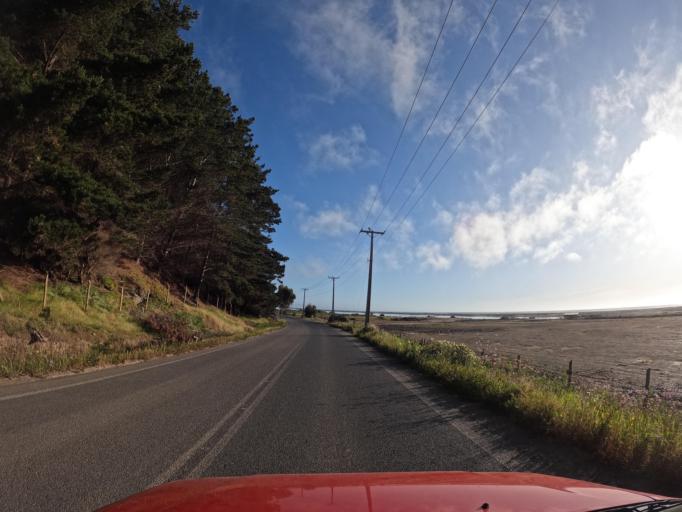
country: CL
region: Maule
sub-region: Provincia de Talca
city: Constitucion
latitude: -34.9885
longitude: -72.1787
